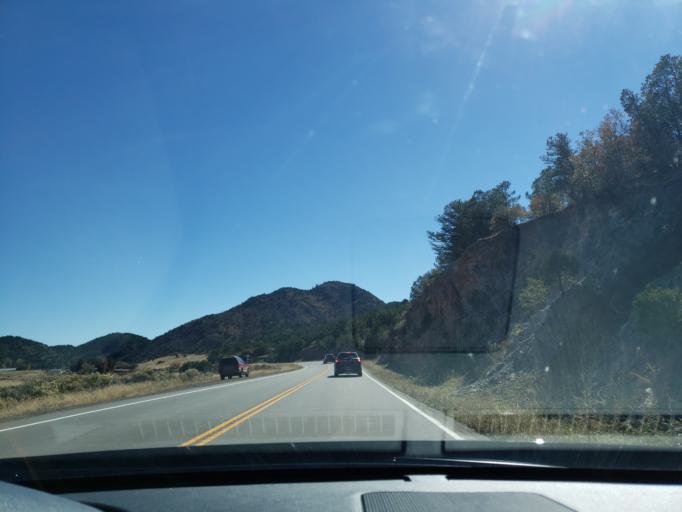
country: US
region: Colorado
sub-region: Fremont County
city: Canon City
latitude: 38.5885
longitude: -105.4223
